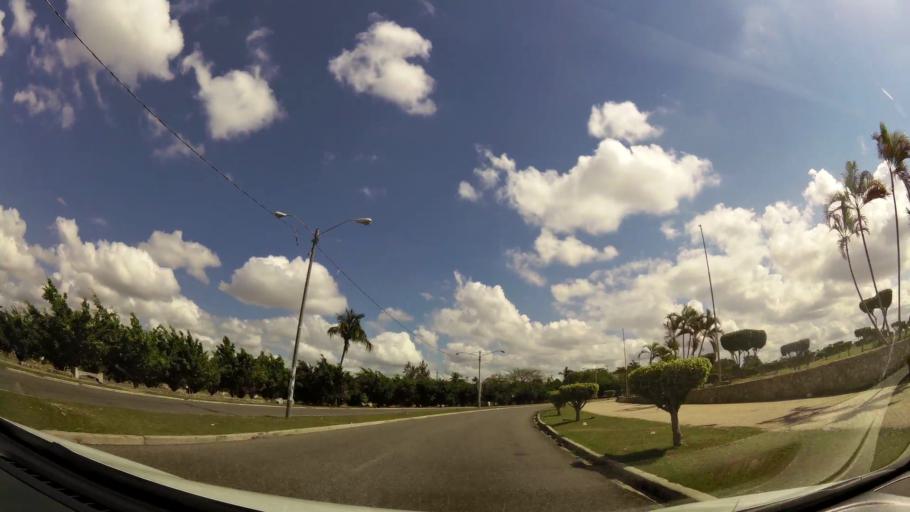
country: DO
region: Santo Domingo
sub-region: Santo Domingo
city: Santo Domingo Este
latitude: 18.4794
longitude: -69.8703
